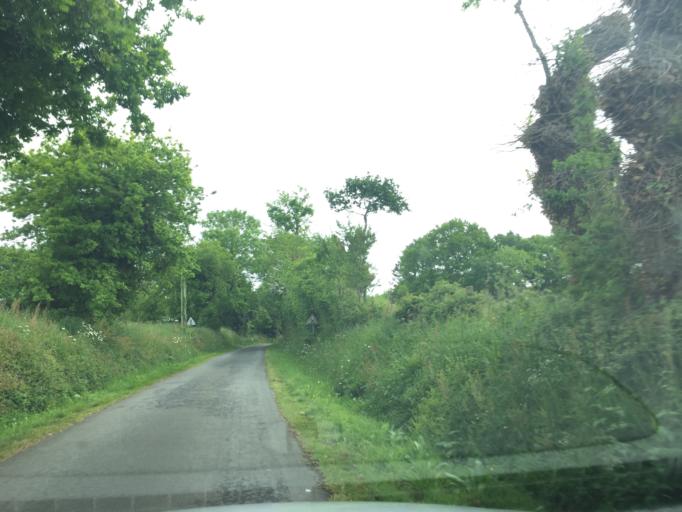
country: FR
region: Brittany
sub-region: Departement des Cotes-d'Armor
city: Saint-Cast-le-Guildo
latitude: 48.5993
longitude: -2.2339
